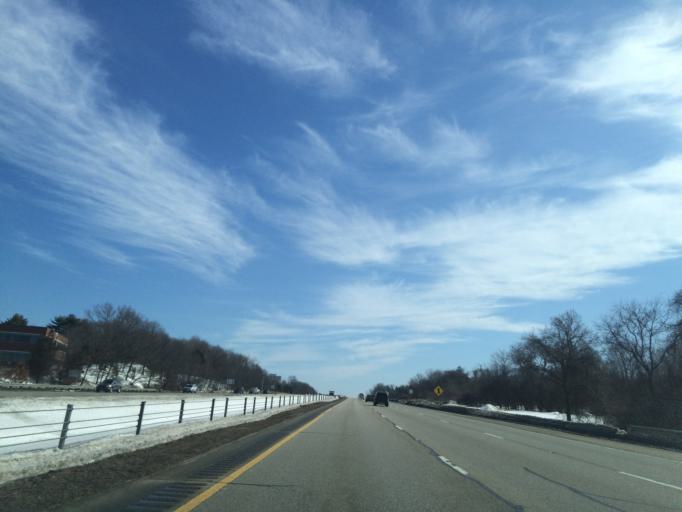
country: US
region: Massachusetts
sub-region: Middlesex County
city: Lexington
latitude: 42.4217
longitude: -71.2358
